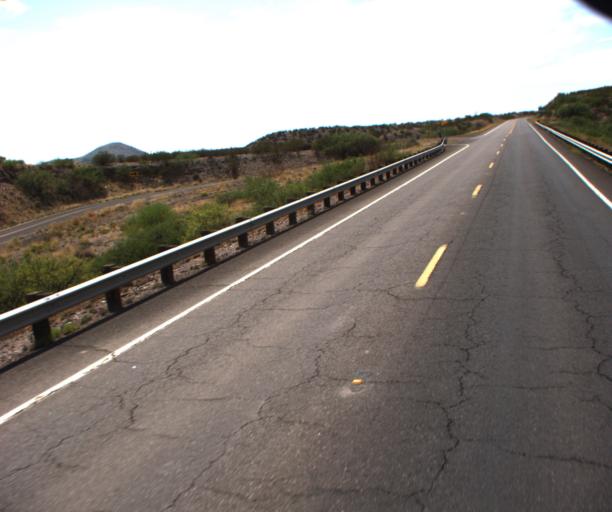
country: US
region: Arizona
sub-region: Greenlee County
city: Clifton
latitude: 32.9418
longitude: -109.2242
